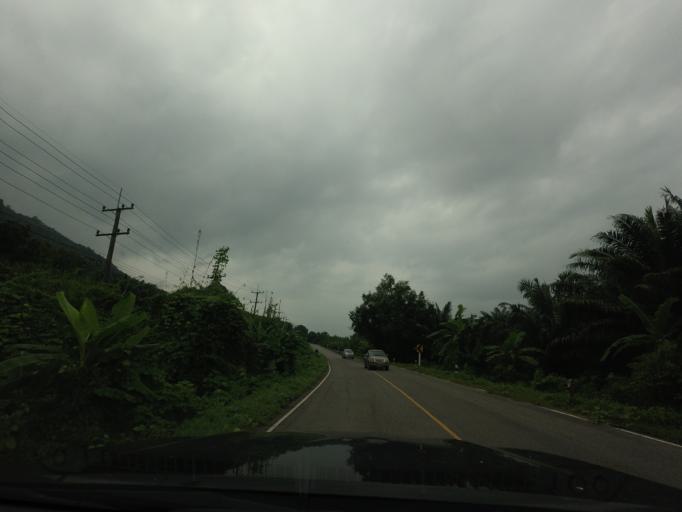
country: TH
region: Nong Khai
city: Sangkhom
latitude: 18.0453
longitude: 102.3316
